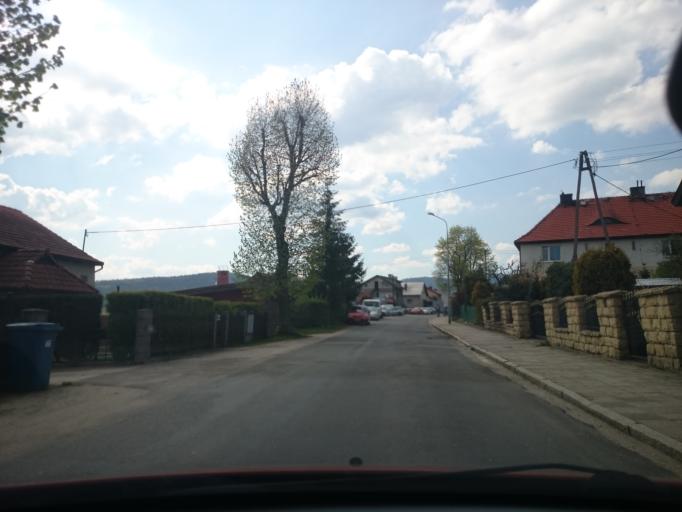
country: PL
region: Lower Silesian Voivodeship
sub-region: Powiat klodzki
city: Bystrzyca Klodzka
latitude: 50.2998
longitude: 16.6395
